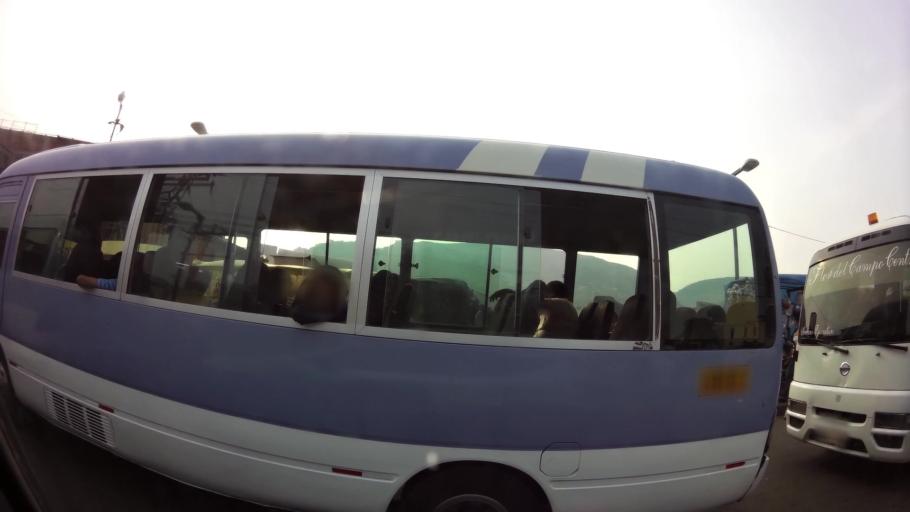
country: HN
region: Francisco Morazan
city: Tegucigalpa
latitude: 14.1036
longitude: -87.2076
